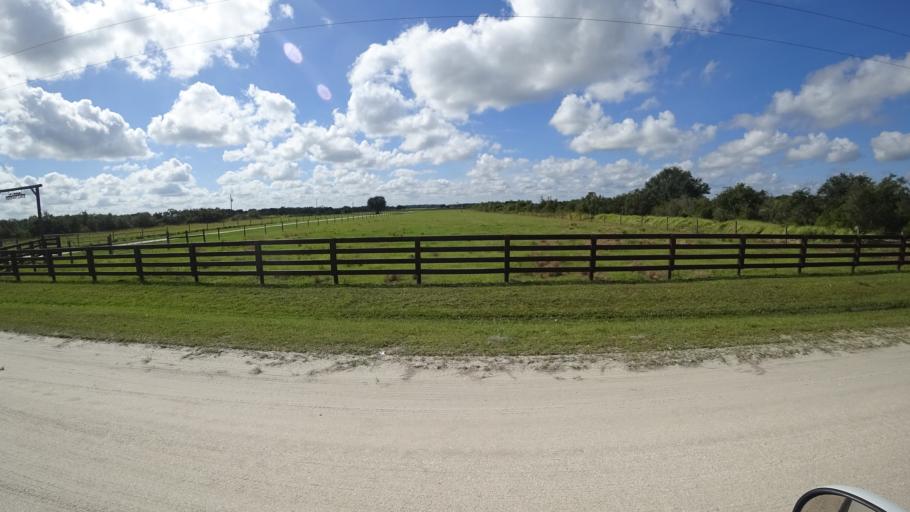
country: US
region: Florida
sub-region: Sarasota County
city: Lake Sarasota
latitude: 27.3655
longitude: -82.1367
